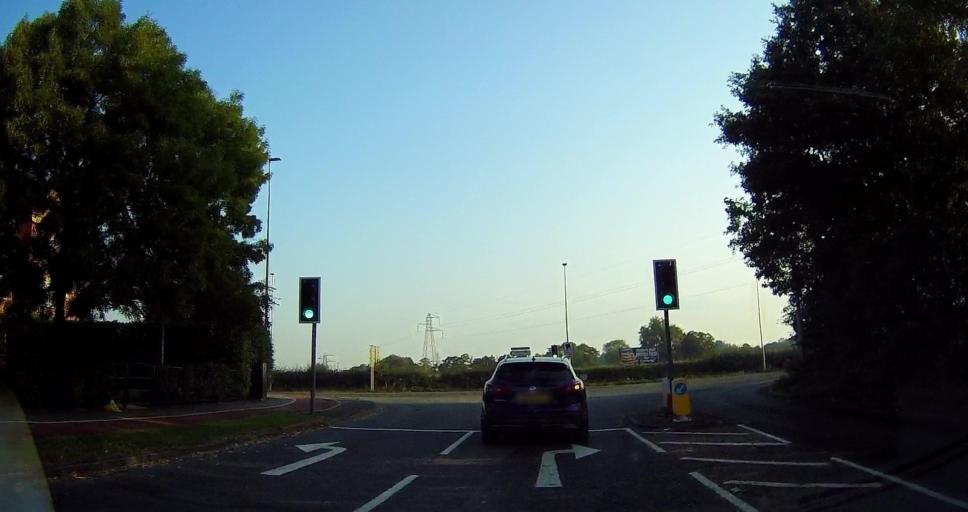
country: GB
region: England
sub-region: Cheshire East
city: Willaston
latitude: 53.0628
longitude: -2.4968
